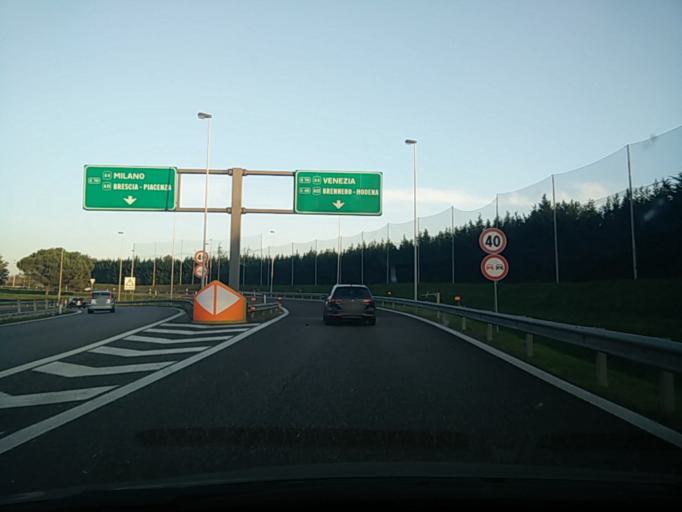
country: IT
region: Veneto
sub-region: Provincia di Verona
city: Cavalcaselle
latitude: 45.4280
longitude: 10.7050
